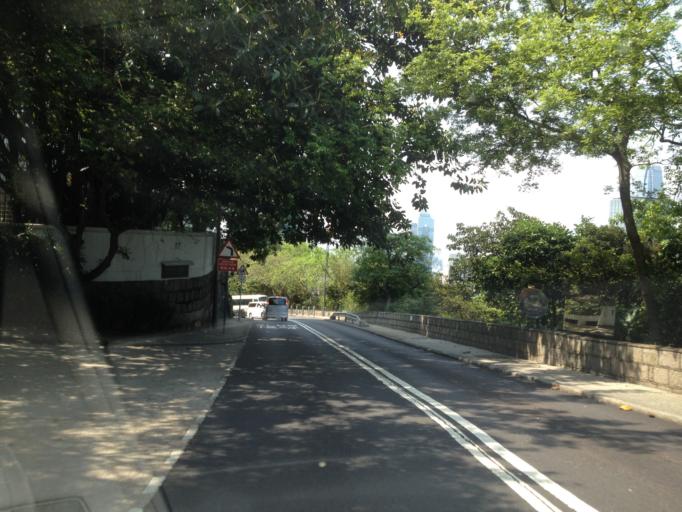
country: HK
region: Central and Western
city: Central
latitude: 22.2725
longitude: 114.1622
